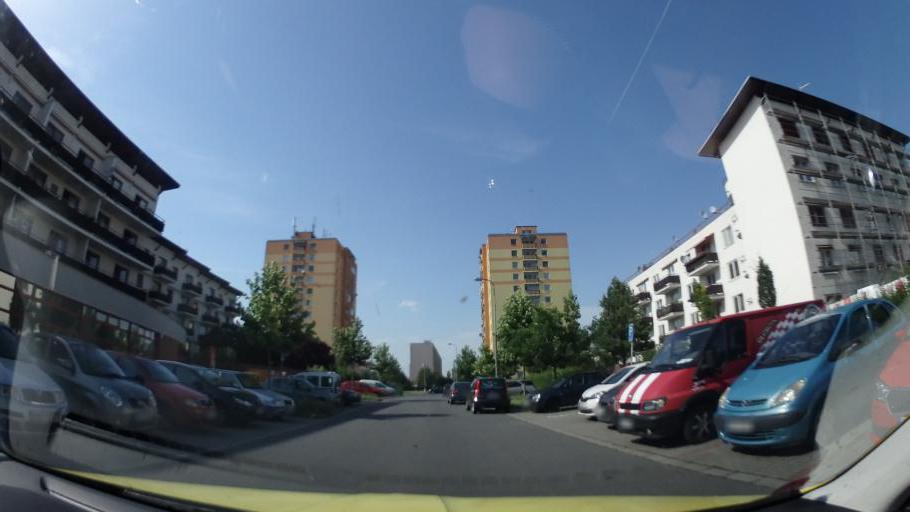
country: CZ
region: Olomoucky
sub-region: Okres Olomouc
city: Olomouc
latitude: 49.5730
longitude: 17.2521
